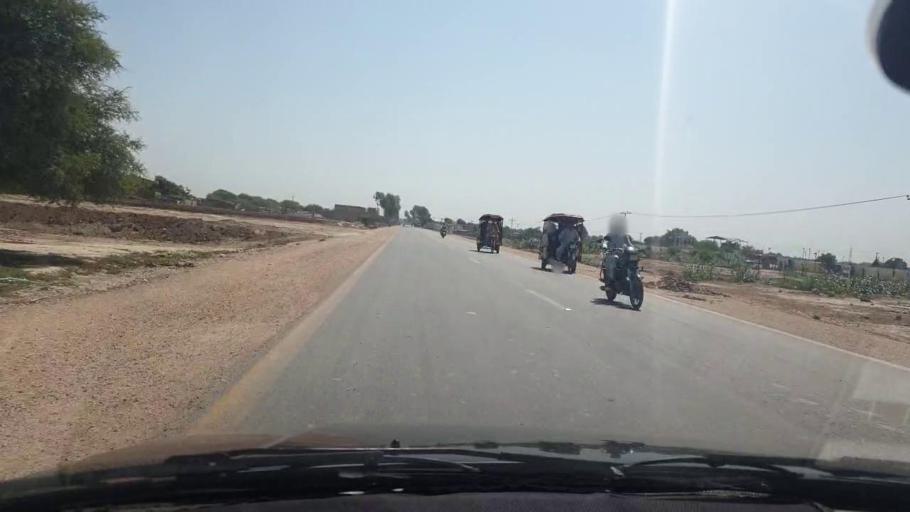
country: PK
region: Sindh
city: Tando Allahyar
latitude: 25.4359
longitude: 68.7421
